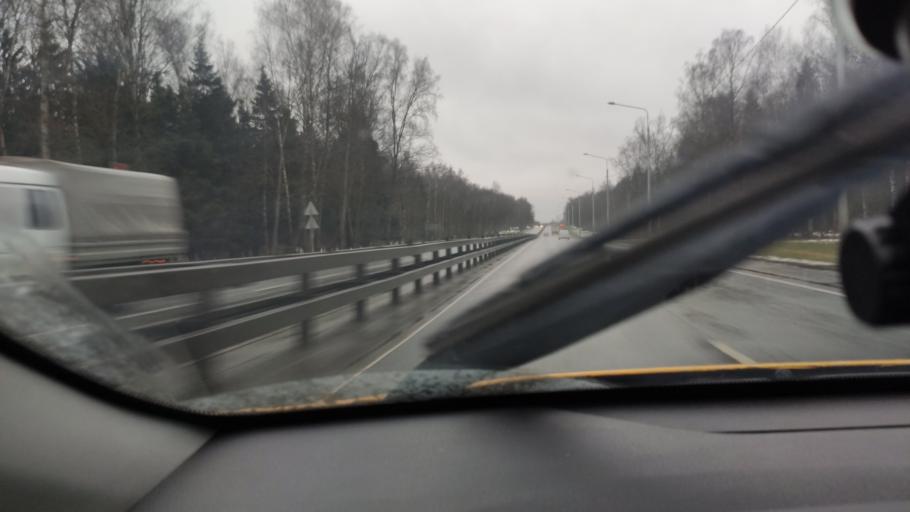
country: RU
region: Moskovskaya
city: Troitsk
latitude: 55.3156
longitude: 37.2435
